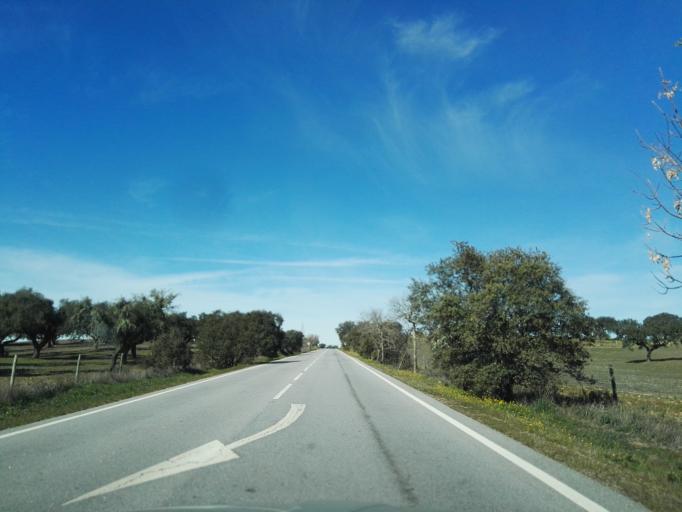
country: PT
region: Portalegre
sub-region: Arronches
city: Arronches
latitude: 39.0767
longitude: -7.2786
